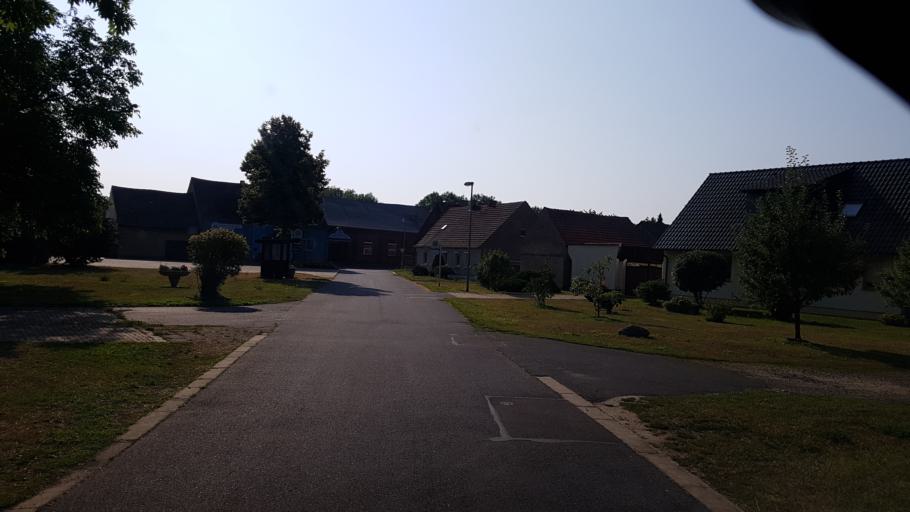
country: DE
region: Brandenburg
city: Drebkau
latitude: 51.6705
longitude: 14.2317
